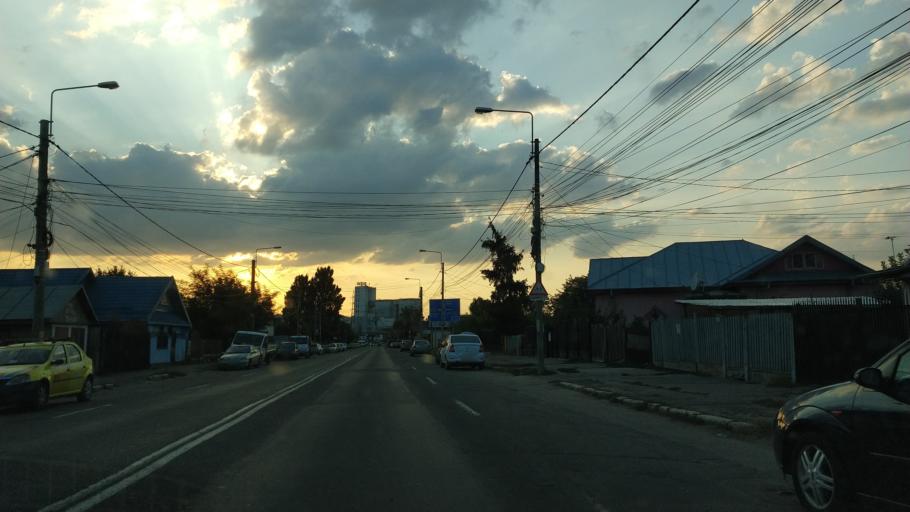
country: RO
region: Buzau
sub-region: Comuna Maracineni
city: Maracineni
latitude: 45.1617
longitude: 26.7942
